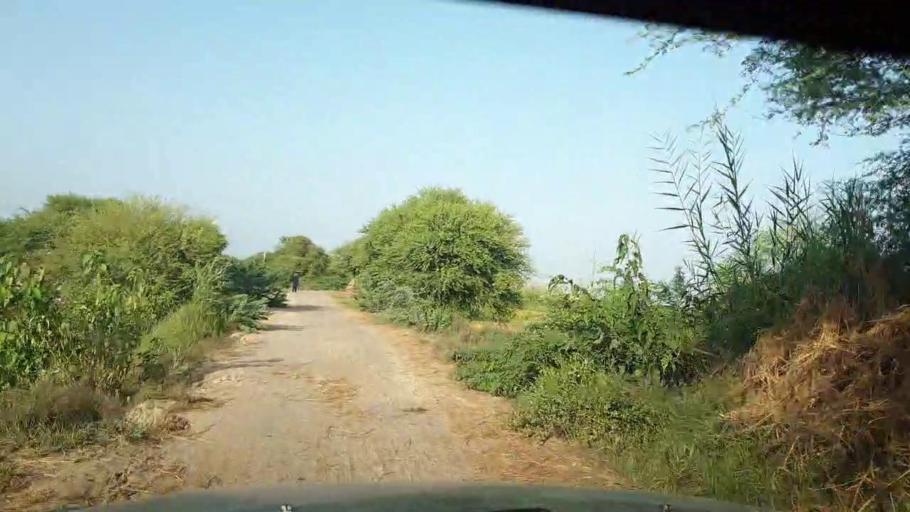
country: PK
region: Sindh
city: Rajo Khanani
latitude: 25.0172
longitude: 68.7635
